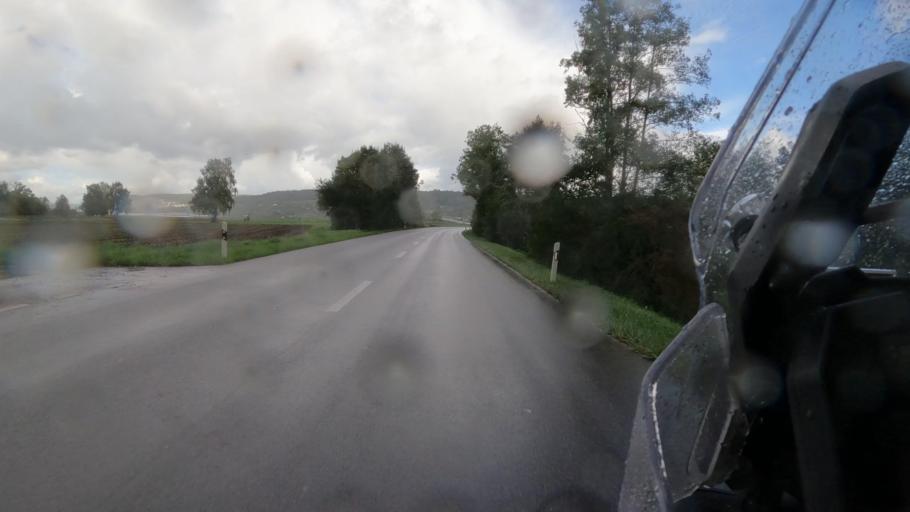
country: CH
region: Zurich
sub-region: Bezirk Andelfingen
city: Marthalen
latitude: 47.6419
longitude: 8.6505
